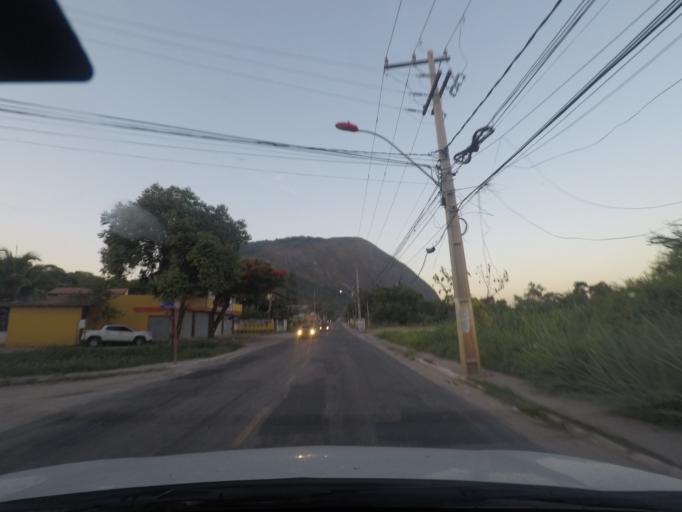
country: BR
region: Rio de Janeiro
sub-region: Marica
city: Marica
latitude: -22.9512
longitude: -42.9622
